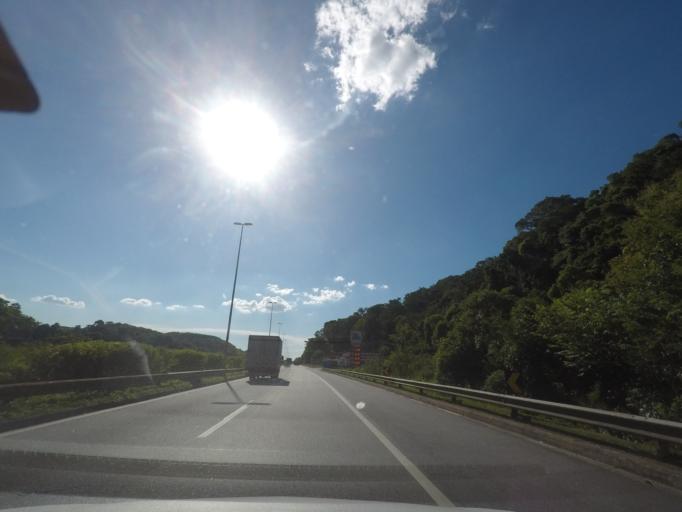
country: BR
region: Rio de Janeiro
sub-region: Petropolis
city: Petropolis
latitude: -22.6537
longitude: -43.1462
